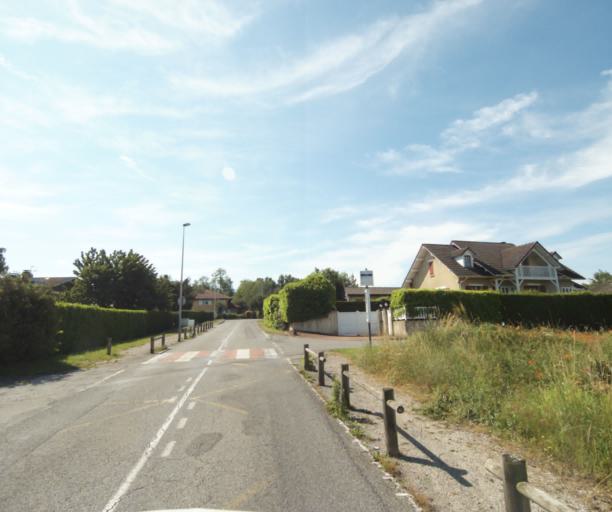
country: FR
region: Rhone-Alpes
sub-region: Departement de la Haute-Savoie
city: Anthy-sur-Leman
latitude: 46.3592
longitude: 6.4410
